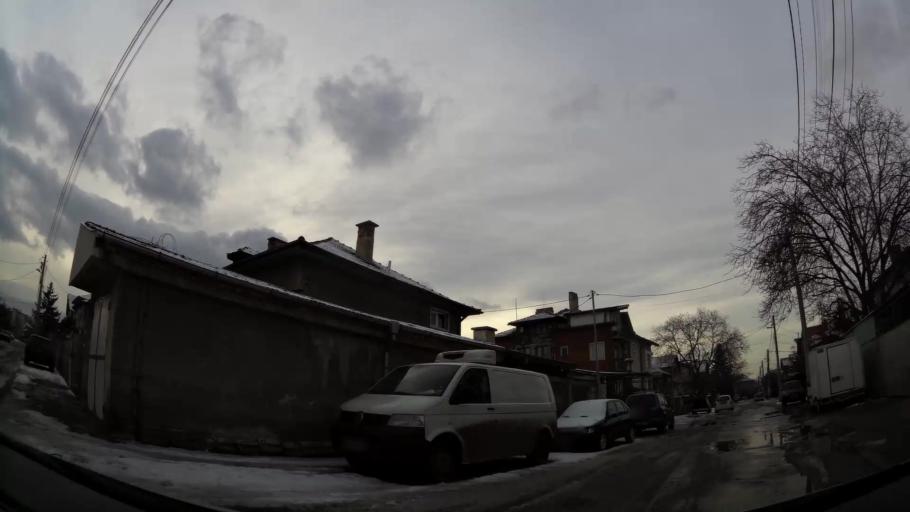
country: BG
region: Sofia-Capital
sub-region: Stolichna Obshtina
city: Sofia
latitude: 42.7271
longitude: 23.3426
